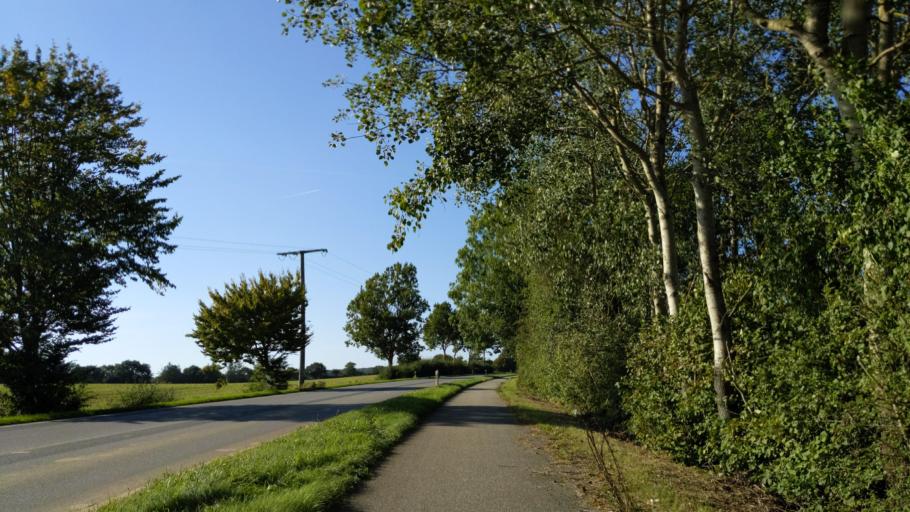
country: DE
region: Schleswig-Holstein
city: Ahrensbok
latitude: 53.9583
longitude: 10.6146
